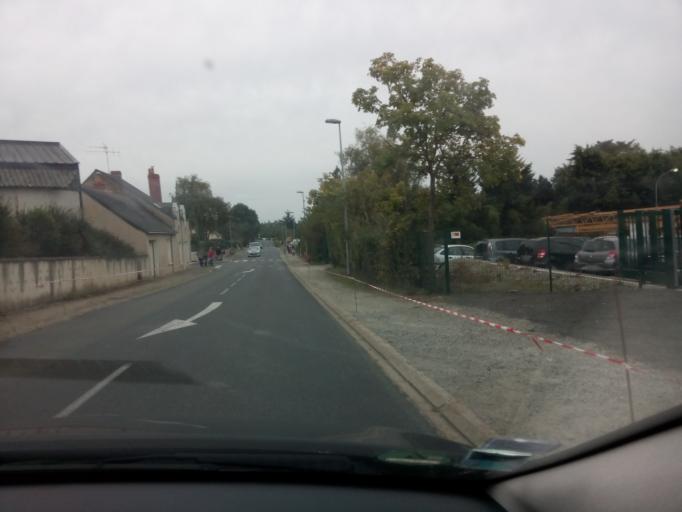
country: FR
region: Pays de la Loire
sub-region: Departement de Maine-et-Loire
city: Soucelles
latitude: 47.6075
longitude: -0.4047
